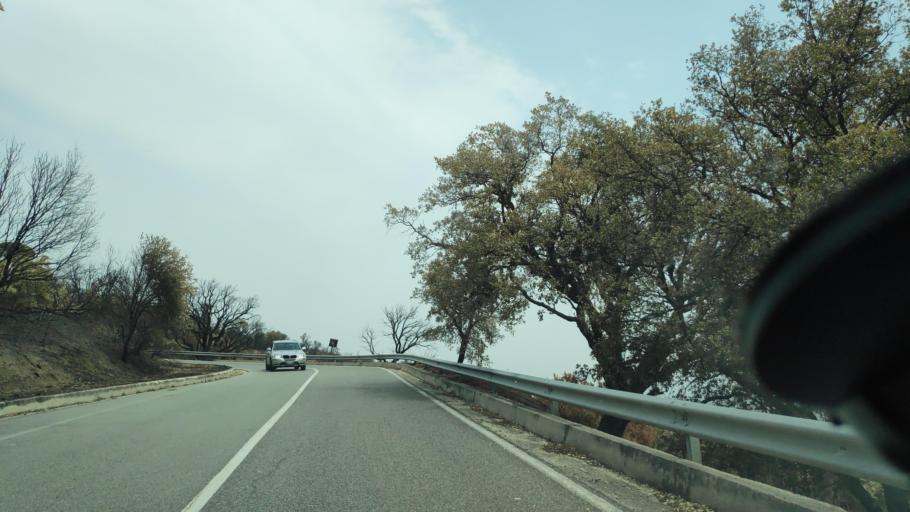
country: IT
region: Calabria
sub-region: Provincia di Catanzaro
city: Sant'Andrea Apostolo dello Ionio
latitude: 38.6403
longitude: 16.5214
